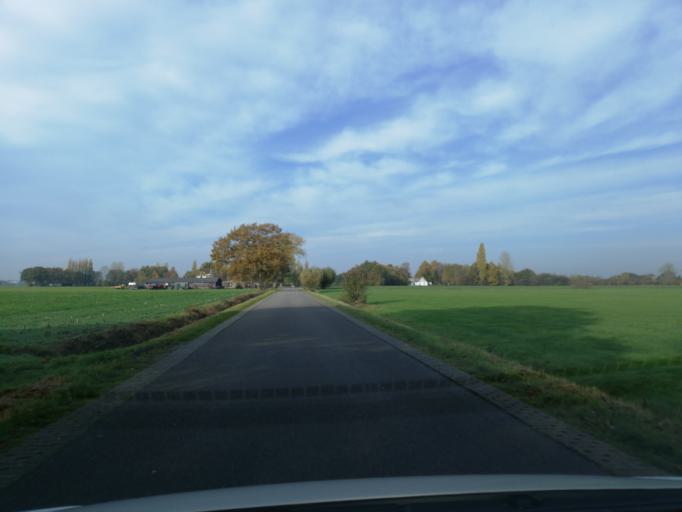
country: NL
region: Gelderland
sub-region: Gemeente Apeldoorn
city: Apeldoorn
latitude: 52.2422
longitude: 6.0276
